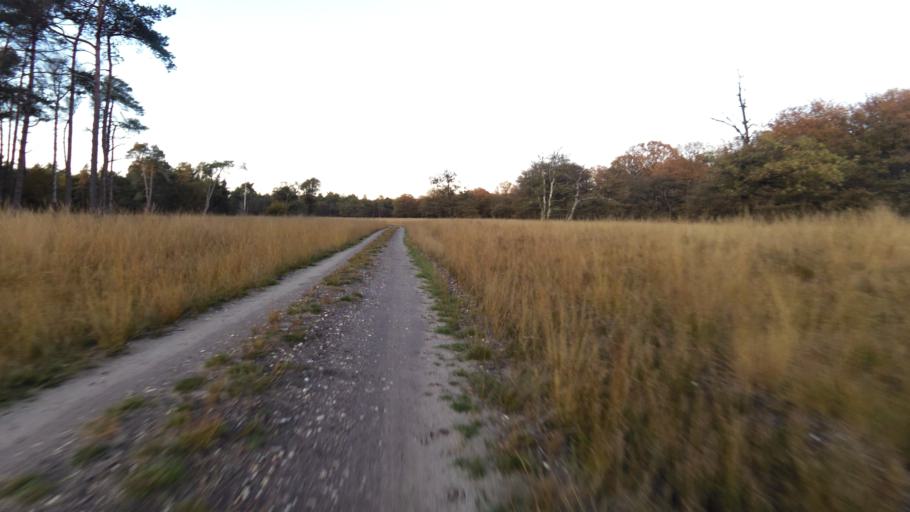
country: NL
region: Gelderland
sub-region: Gemeente Apeldoorn
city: Uddel
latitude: 52.2868
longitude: 5.8375
